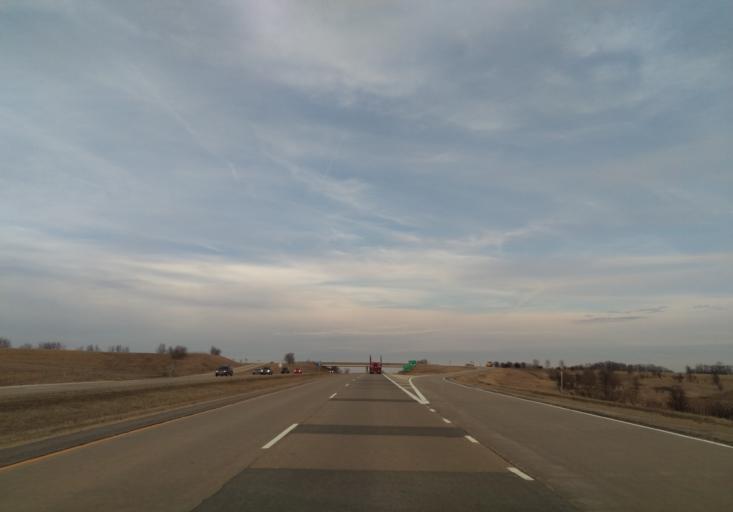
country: US
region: Wisconsin
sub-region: Dane County
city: Verona
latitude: 42.9876
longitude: -89.5881
